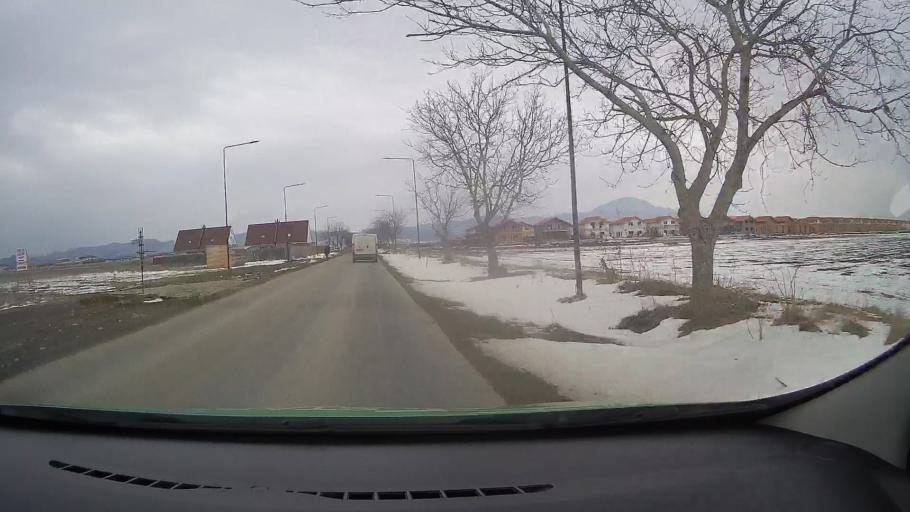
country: RO
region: Brasov
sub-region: Comuna Cristian
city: Cristian
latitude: 45.6289
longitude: 25.4673
